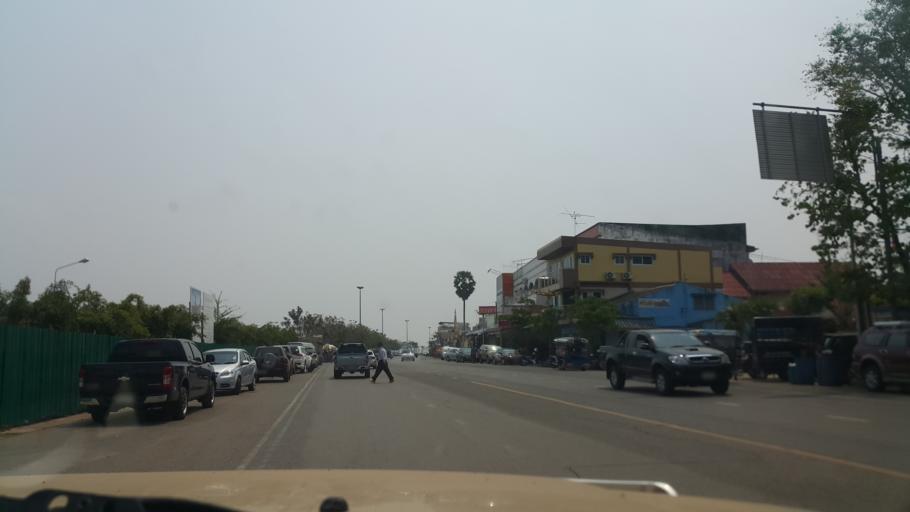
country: TH
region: Nakhon Phanom
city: Nakhon Phanom
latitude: 17.3989
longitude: 104.7904
